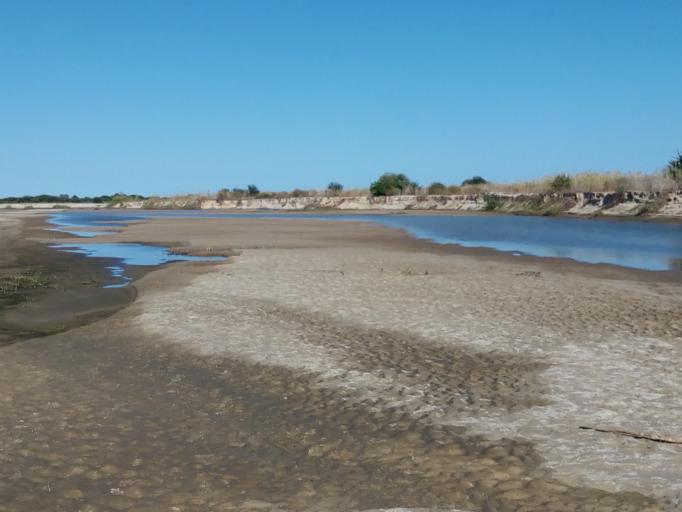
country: MG
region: Menabe
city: Morondava
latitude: -20.3359
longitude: 44.3115
